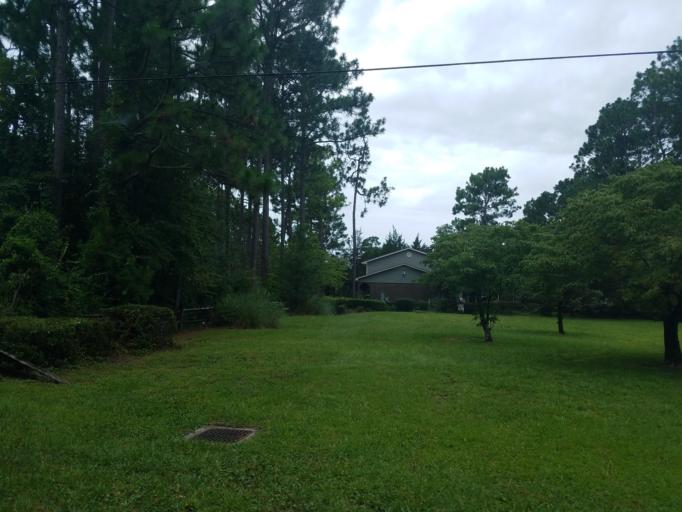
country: US
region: North Carolina
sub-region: New Hanover County
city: Kings Grant
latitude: 34.2405
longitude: -77.8599
